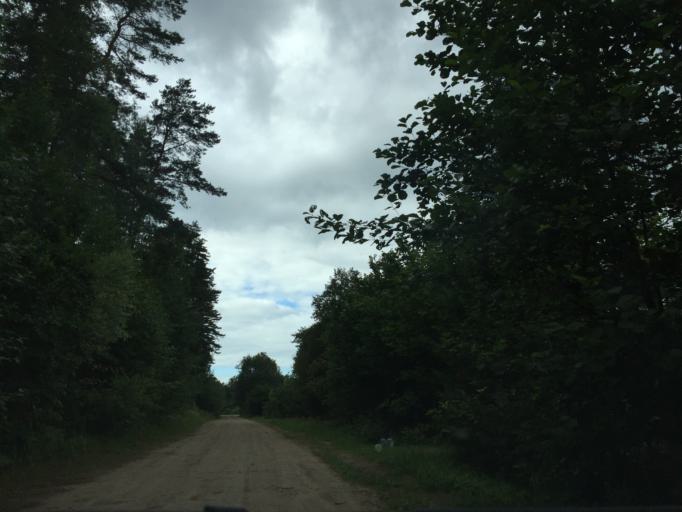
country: LV
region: Saulkrastu
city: Saulkrasti
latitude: 57.2359
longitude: 24.4626
